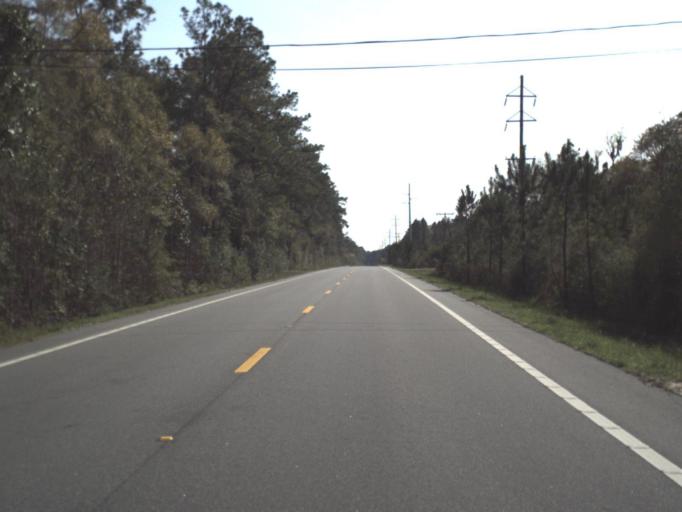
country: US
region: Florida
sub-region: Wakulla County
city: Crawfordville
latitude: 30.0191
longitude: -84.5004
